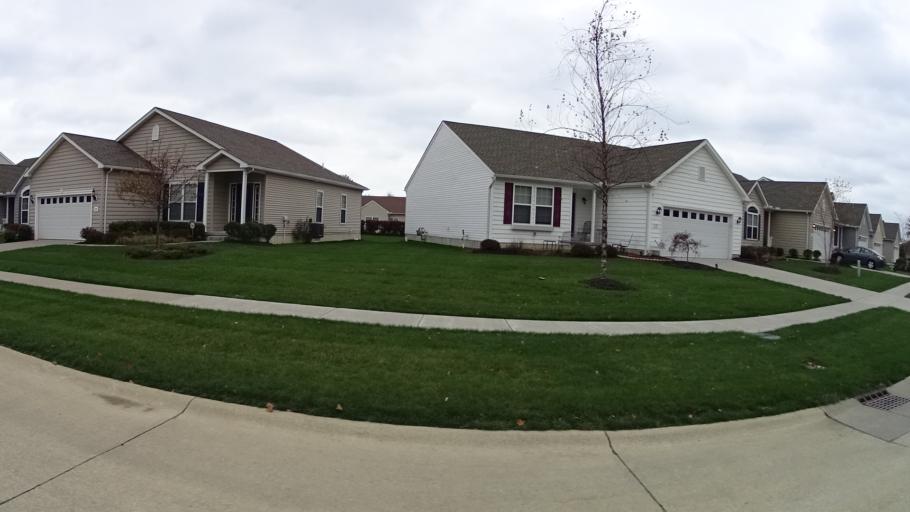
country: US
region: Ohio
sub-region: Lorain County
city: Amherst
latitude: 41.4371
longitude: -82.2272
